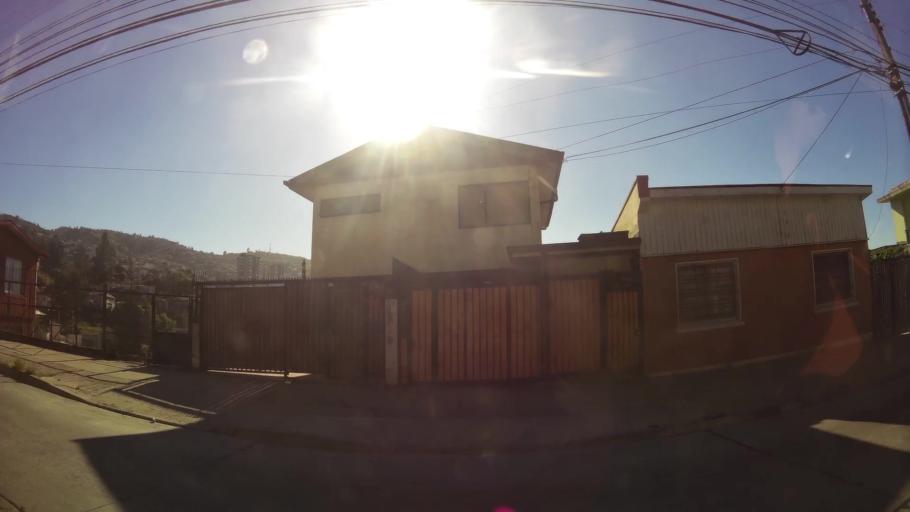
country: CL
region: Valparaiso
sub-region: Provincia de Valparaiso
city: Valparaiso
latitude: -33.0533
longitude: -71.6196
